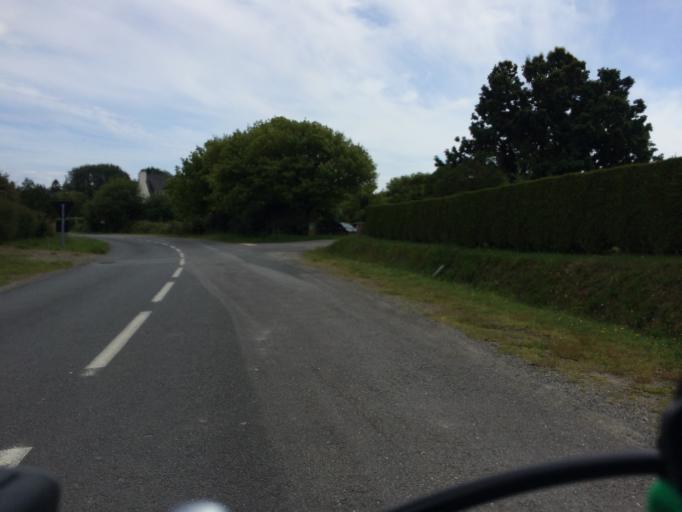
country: FR
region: Brittany
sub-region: Departement du Finistere
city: Logonna-Daoulas
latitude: 48.3224
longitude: -4.2971
